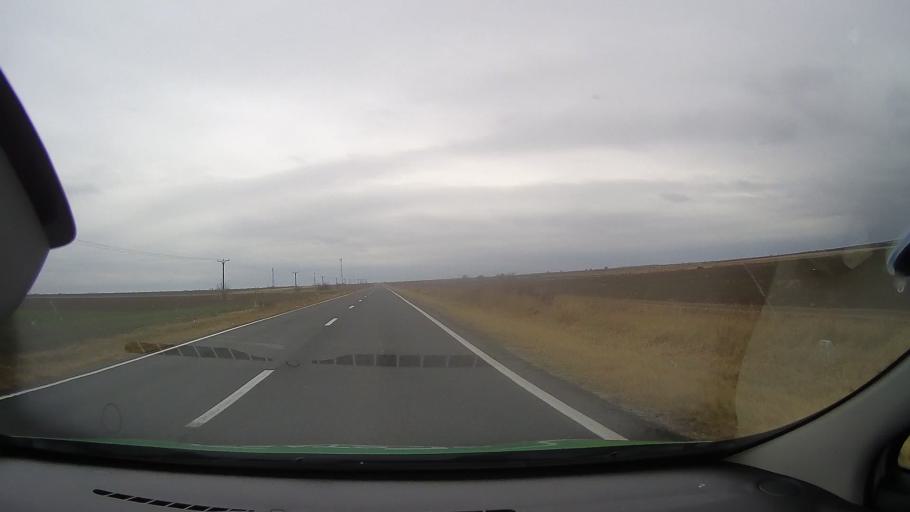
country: RO
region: Constanta
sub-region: Comuna Nicolae Balcescu
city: Nicolae Balcescu
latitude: 44.3771
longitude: 28.4179
